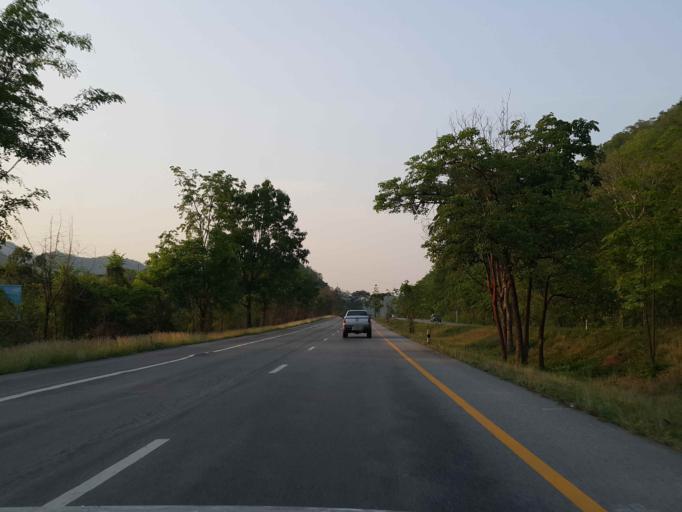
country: TH
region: Lampang
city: Sop Prap
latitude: 17.8203
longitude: 99.2828
